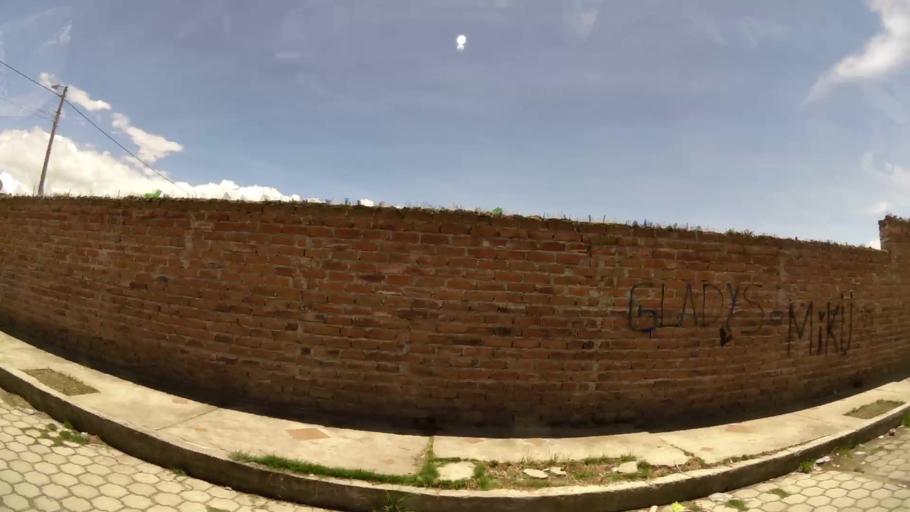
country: EC
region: Chimborazo
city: Riobamba
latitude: -1.6834
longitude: -78.6518
